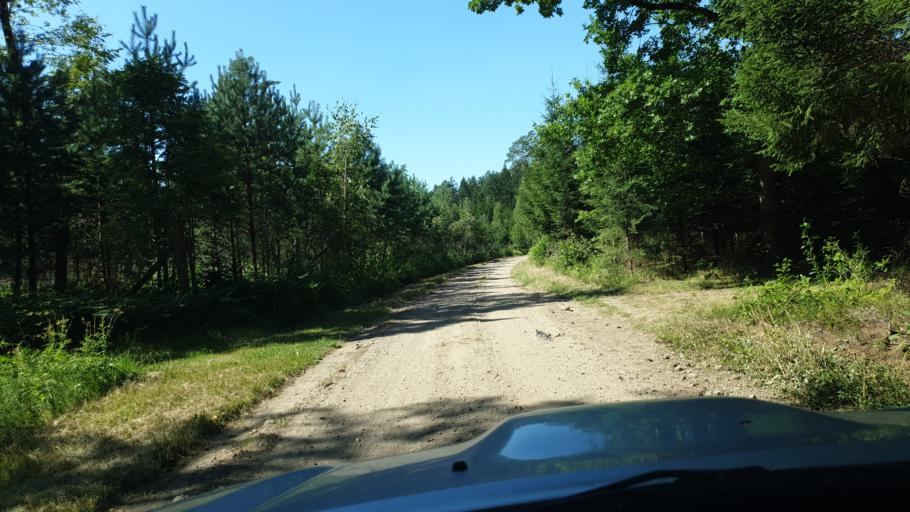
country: LT
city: Sirvintos
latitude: 54.9072
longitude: 24.9433
